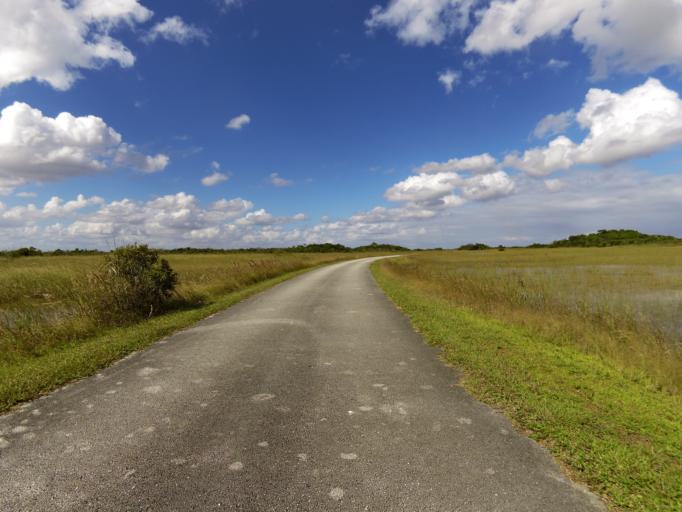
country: US
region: Florida
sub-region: Miami-Dade County
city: The Hammocks
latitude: 25.7191
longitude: -80.7625
